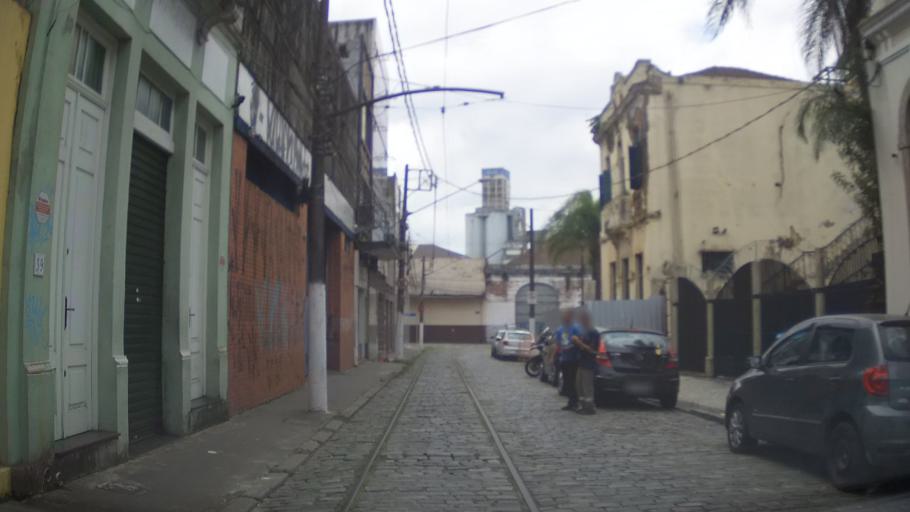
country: BR
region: Sao Paulo
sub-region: Santos
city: Santos
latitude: -23.9332
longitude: -46.3231
